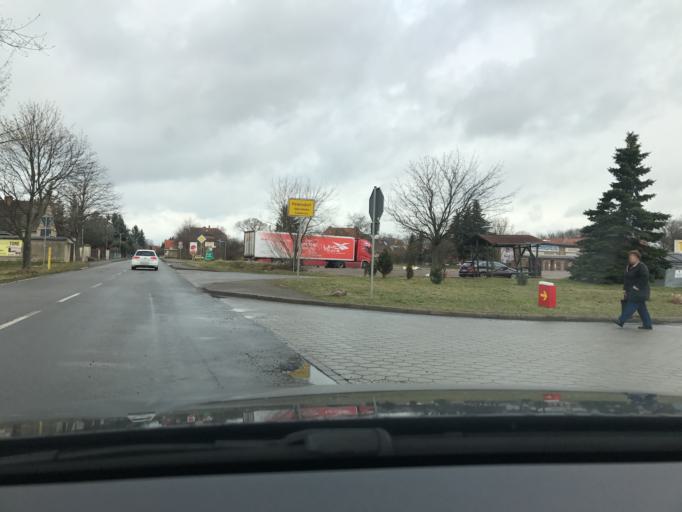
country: DE
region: Saxony-Anhalt
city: Landsberg
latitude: 51.5355
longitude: 12.1367
